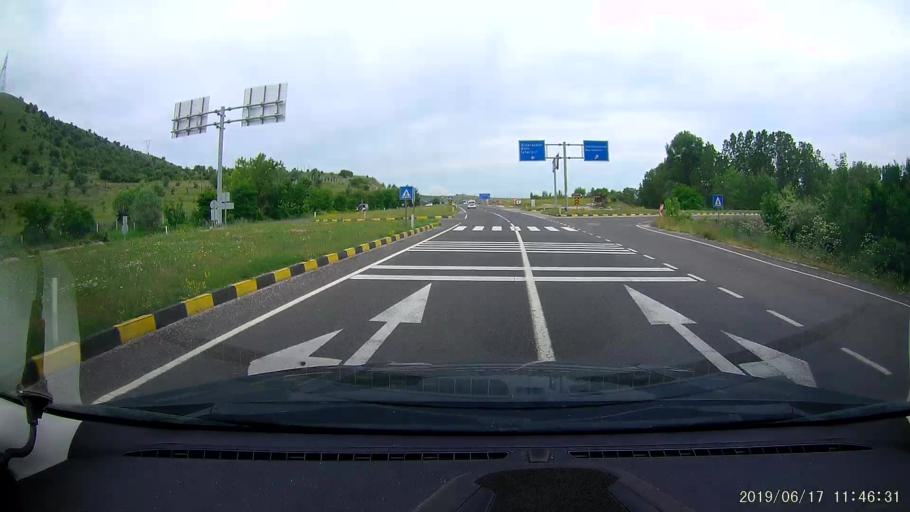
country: TR
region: Cankiri
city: Kursunlu
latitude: 40.8492
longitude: 33.2279
